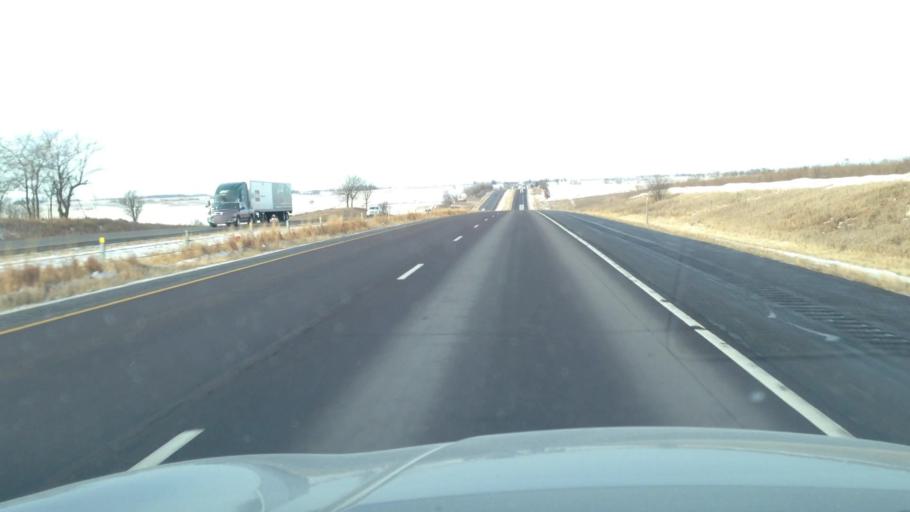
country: US
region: Iowa
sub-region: Poweshiek County
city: Grinnell
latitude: 41.6958
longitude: -92.6589
